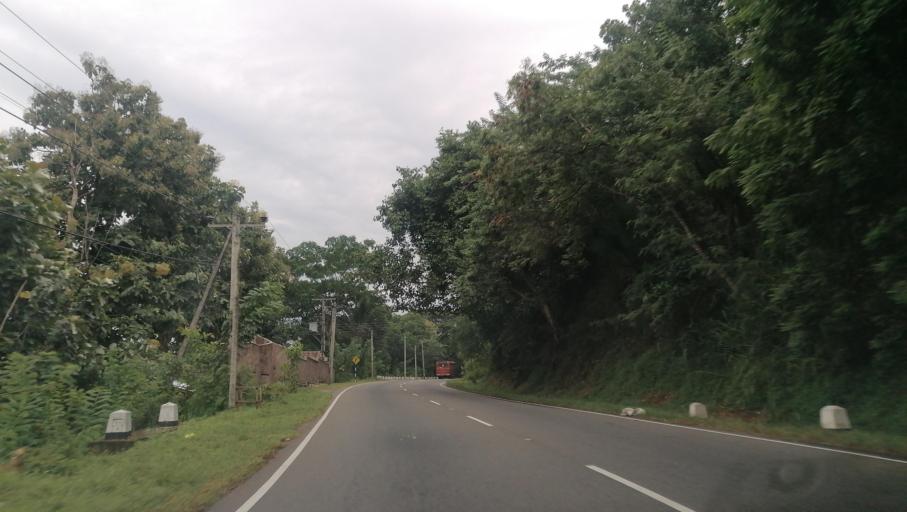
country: LK
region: Central
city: Kandy
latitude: 7.2436
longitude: 80.7272
